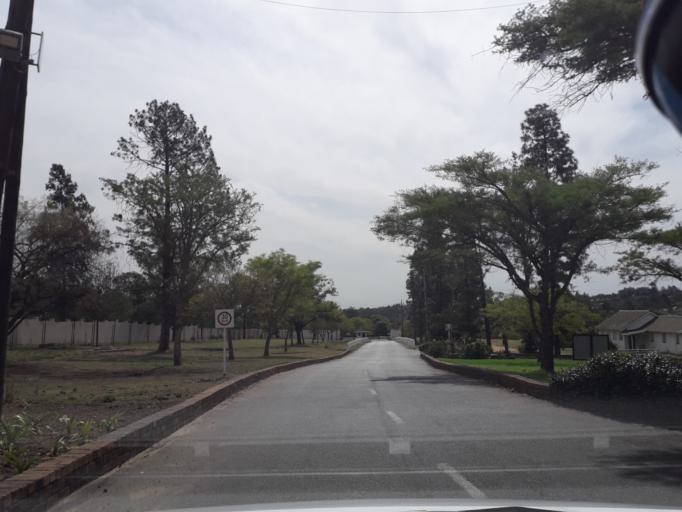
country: ZA
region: Gauteng
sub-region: City of Johannesburg Metropolitan Municipality
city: Diepsloot
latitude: -25.9787
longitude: 28.0579
